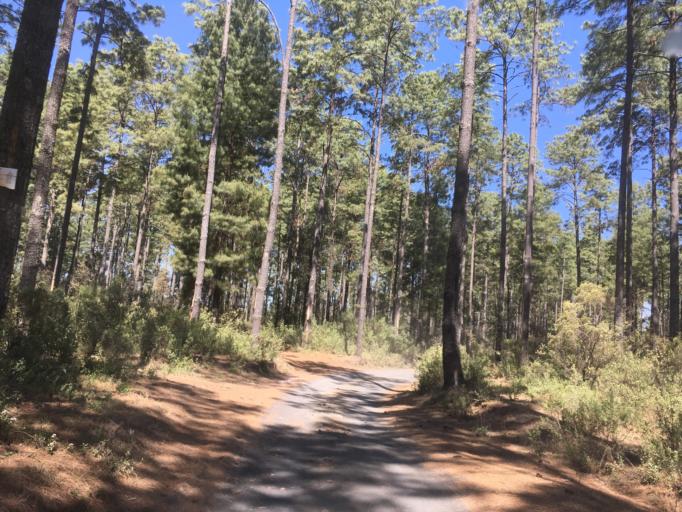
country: MX
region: Michoacan
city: Angahuan
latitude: 19.4616
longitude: -102.2127
